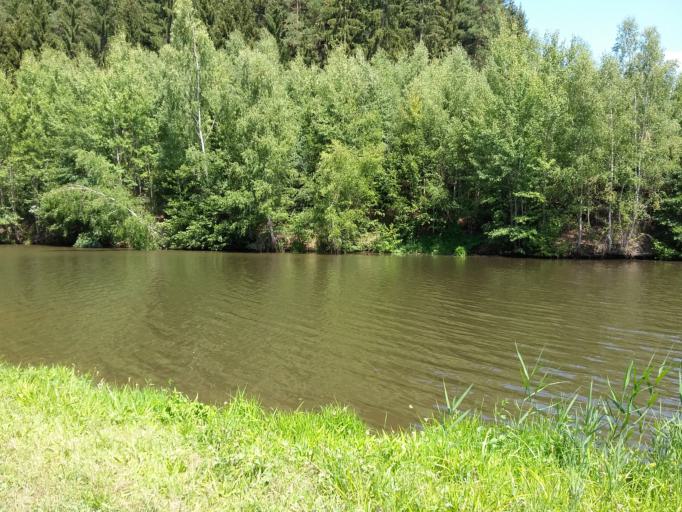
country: CZ
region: Pardubicky
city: Letohrad
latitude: 50.0248
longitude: 16.4646
